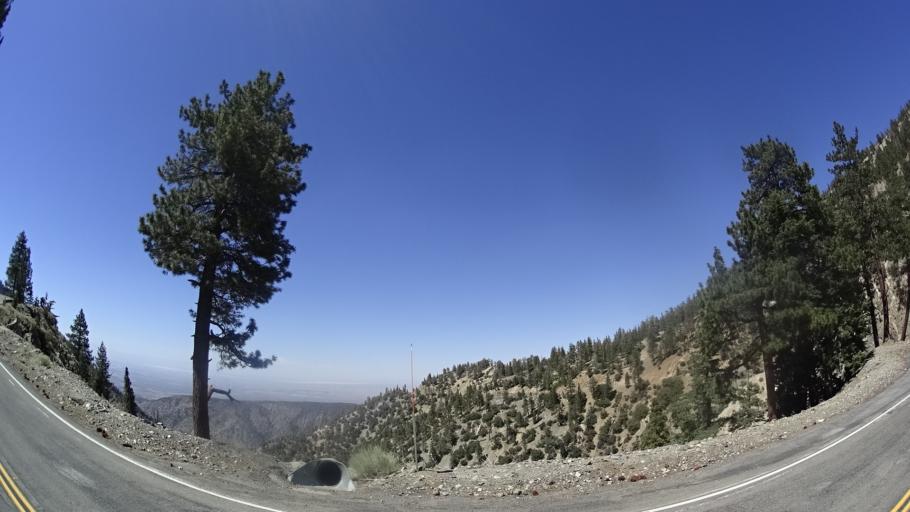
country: US
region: California
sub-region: San Bernardino County
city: Wrightwood
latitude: 34.3676
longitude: -117.7838
